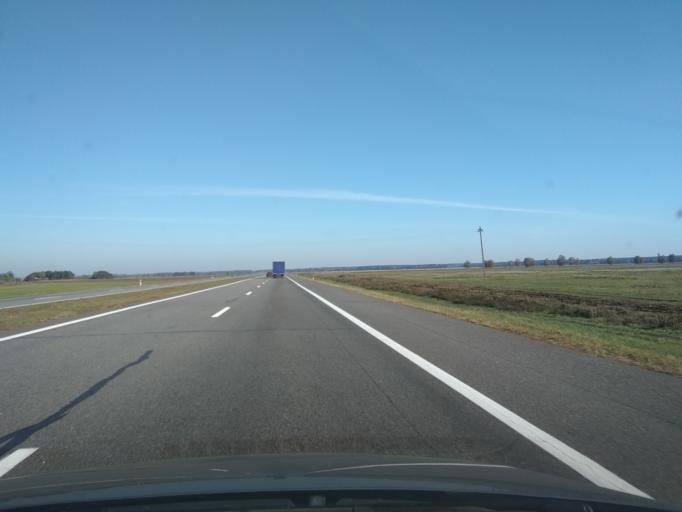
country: BY
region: Brest
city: Ivatsevichy
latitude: 52.7248
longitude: 25.4384
